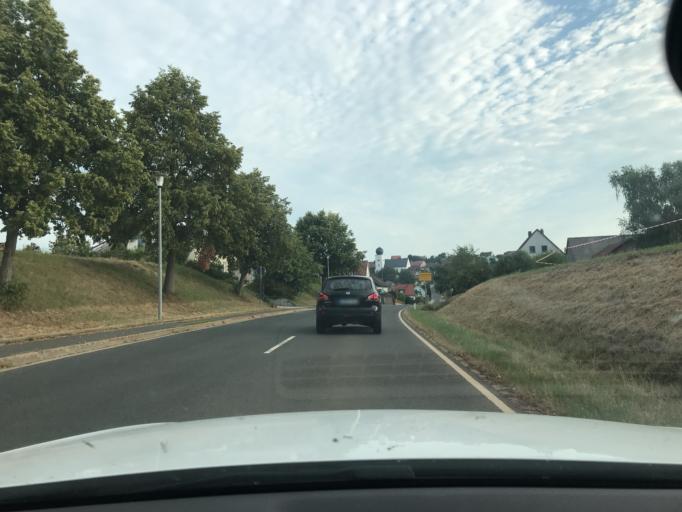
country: DE
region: Bavaria
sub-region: Upper Franconia
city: Pegnitz
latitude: 49.7620
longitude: 11.6021
